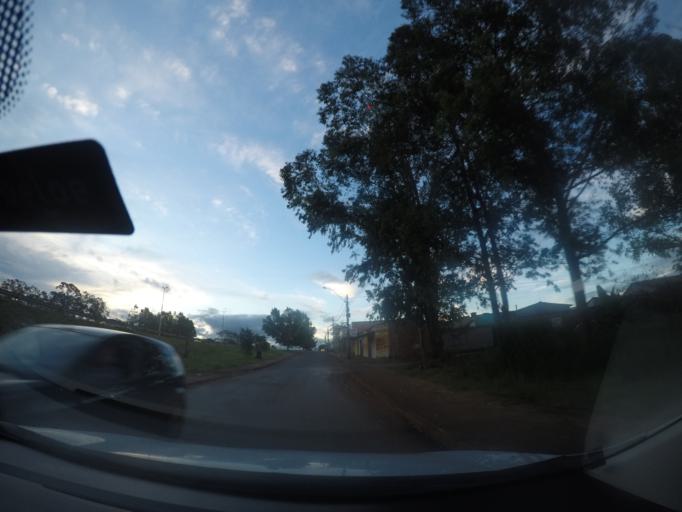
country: BR
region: Goias
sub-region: Goianira
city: Goianira
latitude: -16.5709
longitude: -49.3946
